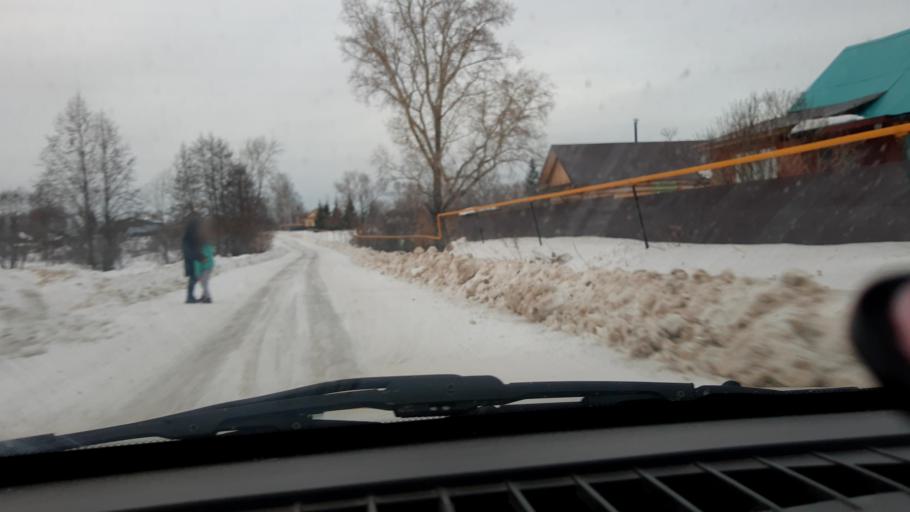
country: RU
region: Bashkortostan
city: Urman
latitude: 54.8720
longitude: 56.8709
